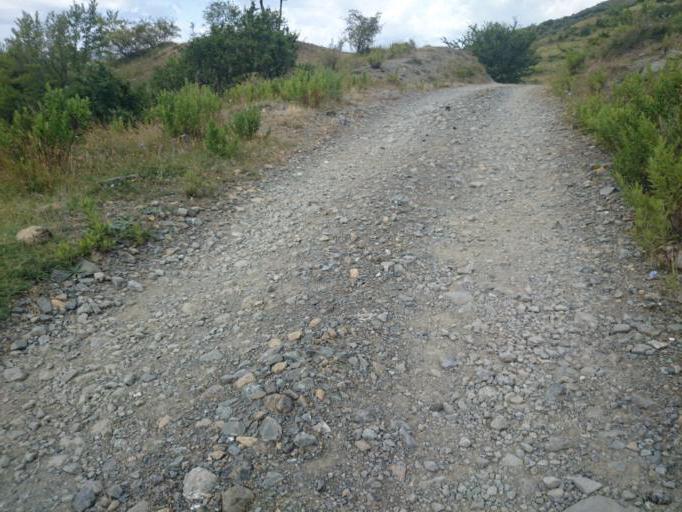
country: AL
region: Elbasan
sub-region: Rrethi i Gramshit
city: Lenias
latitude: 40.7772
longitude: 20.3773
